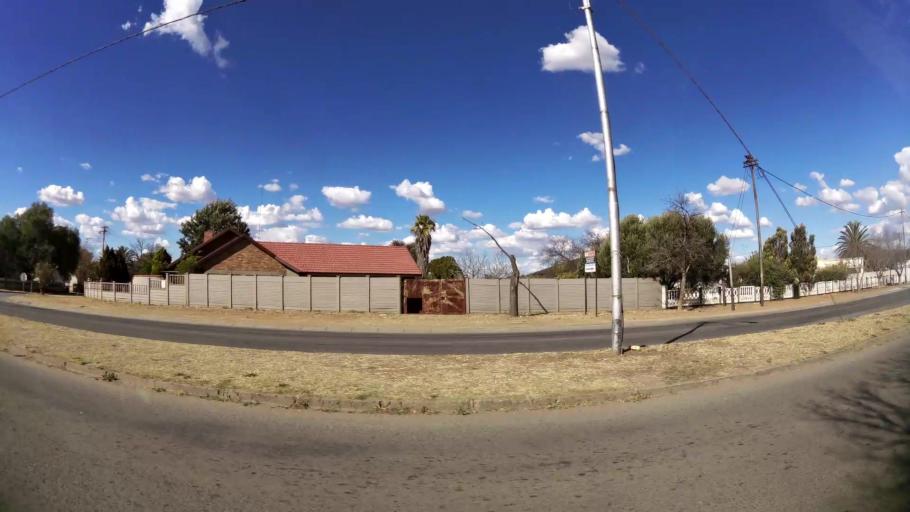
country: ZA
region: North-West
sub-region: Dr Kenneth Kaunda District Municipality
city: Klerksdorp
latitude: -26.8642
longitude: 26.6411
